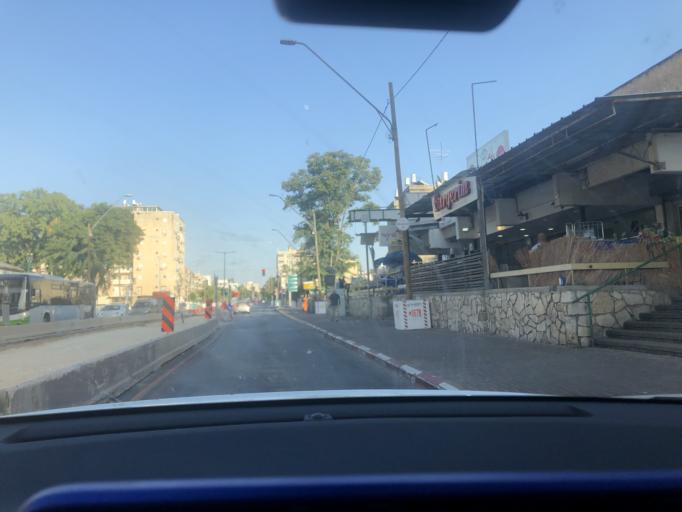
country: IL
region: Central District
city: Lod
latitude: 31.9502
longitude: 34.8873
